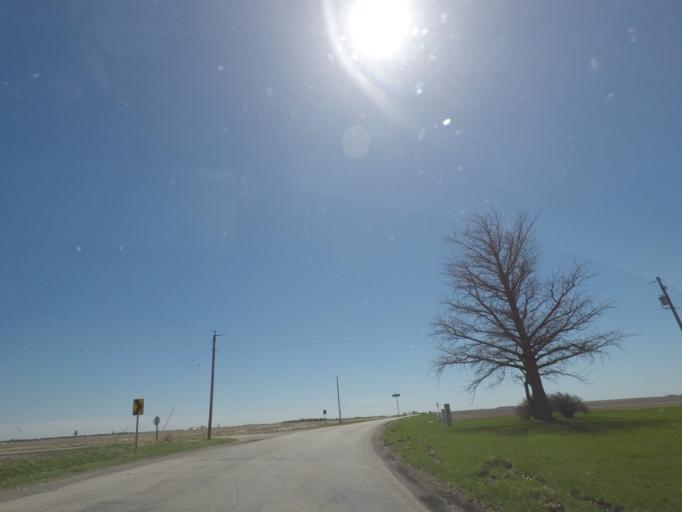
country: US
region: Illinois
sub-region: Logan County
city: Atlanta
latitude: 40.2588
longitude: -89.2054
